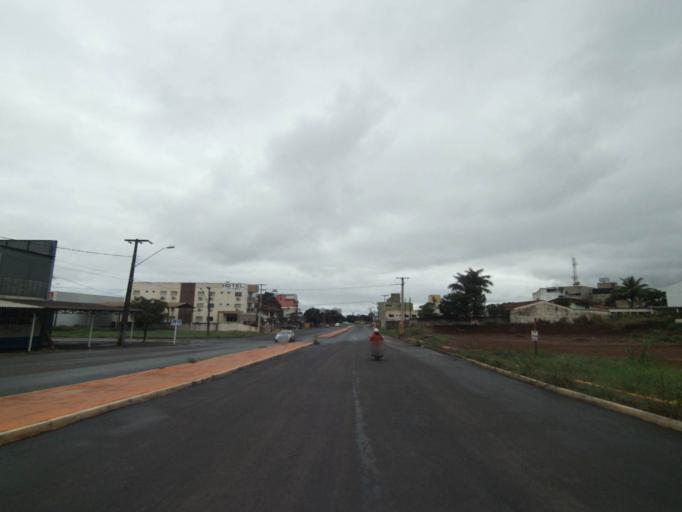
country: BR
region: Parana
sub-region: Foz Do Iguacu
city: Foz do Iguacu
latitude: -25.5173
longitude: -54.5612
